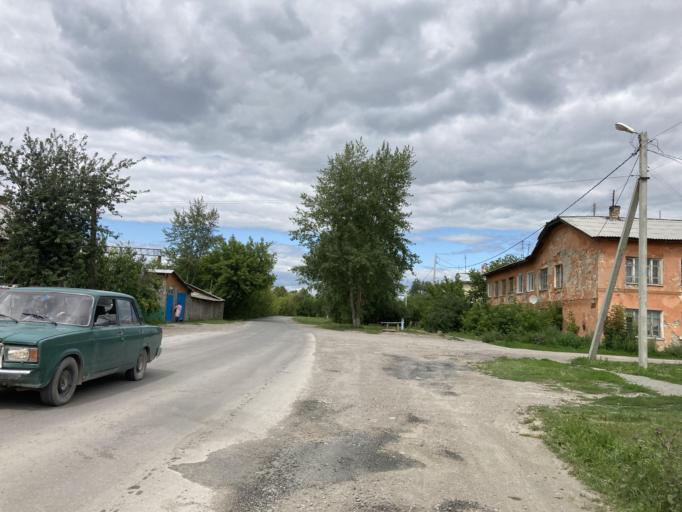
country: RU
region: Sverdlovsk
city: Bogdanovich
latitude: 56.7847
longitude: 62.0665
